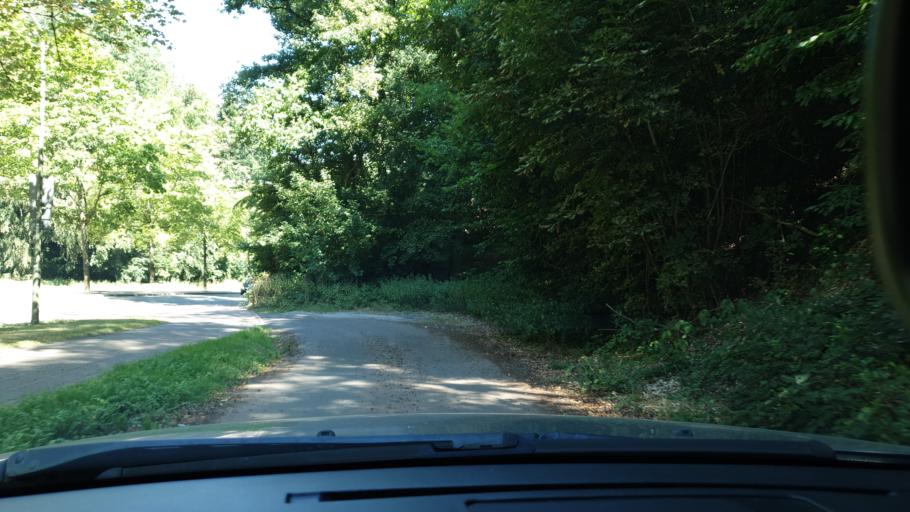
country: DE
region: Rheinland-Pfalz
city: Kaiserslautern
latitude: 49.4578
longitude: 7.7614
